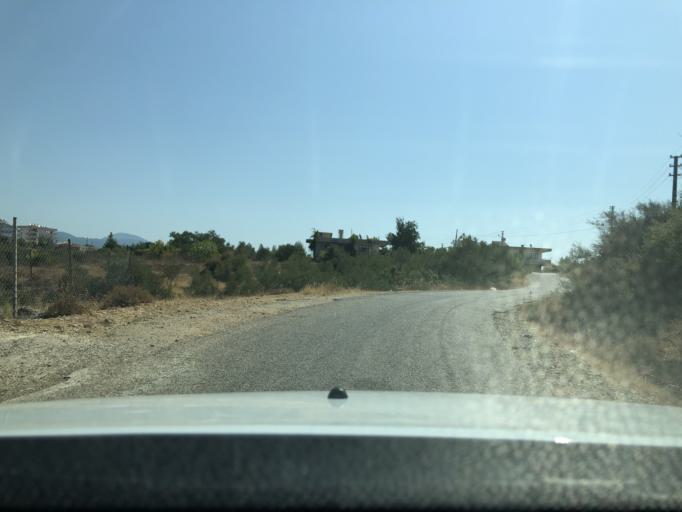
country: TR
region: Antalya
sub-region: Manavgat
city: Manavgat
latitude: 36.8044
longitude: 31.4715
